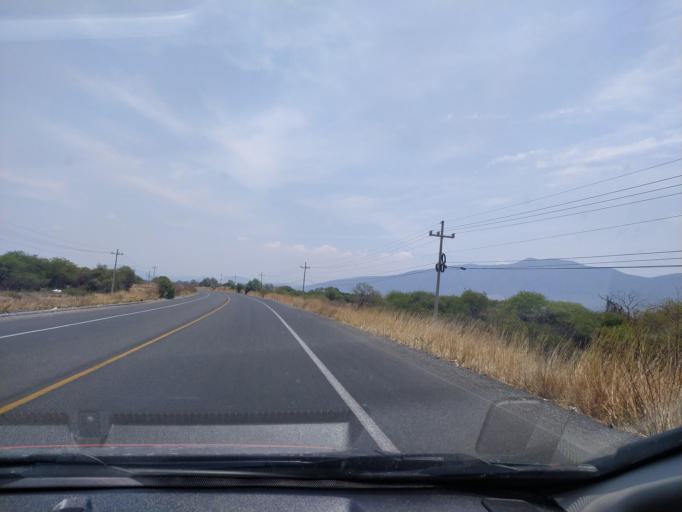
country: MX
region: Jalisco
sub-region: Zacoalco de Torres
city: Barranca de Otates (Barranca de Otatan)
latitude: 20.3172
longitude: -103.5902
